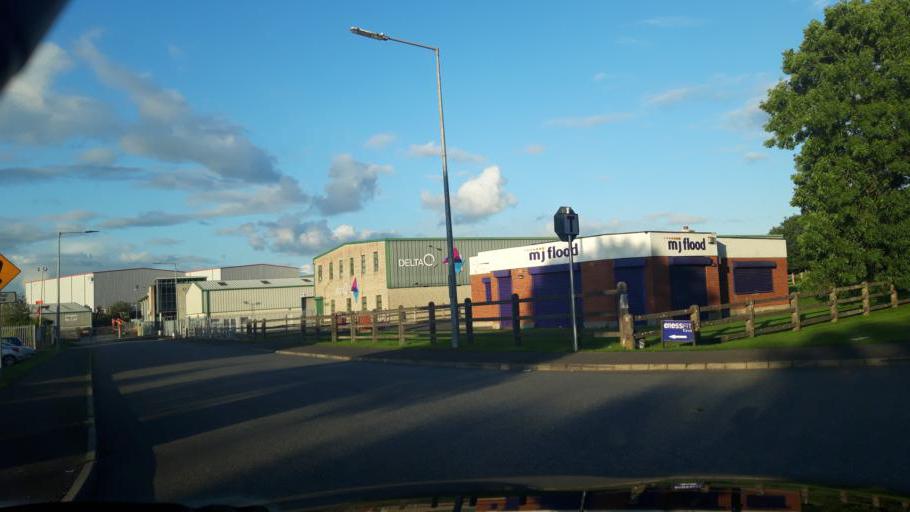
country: IE
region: Leinster
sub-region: An Iarmhi
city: Athlone
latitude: 53.4267
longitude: -7.8992
